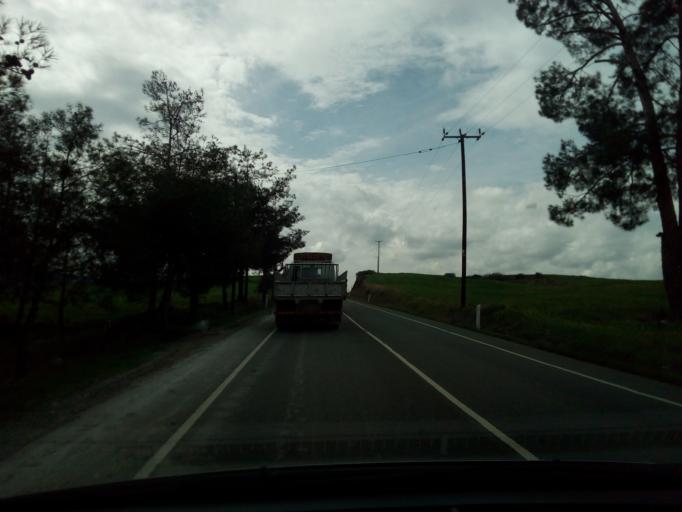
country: CY
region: Lefkosia
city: Kakopetria
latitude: 35.0742
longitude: 32.9438
